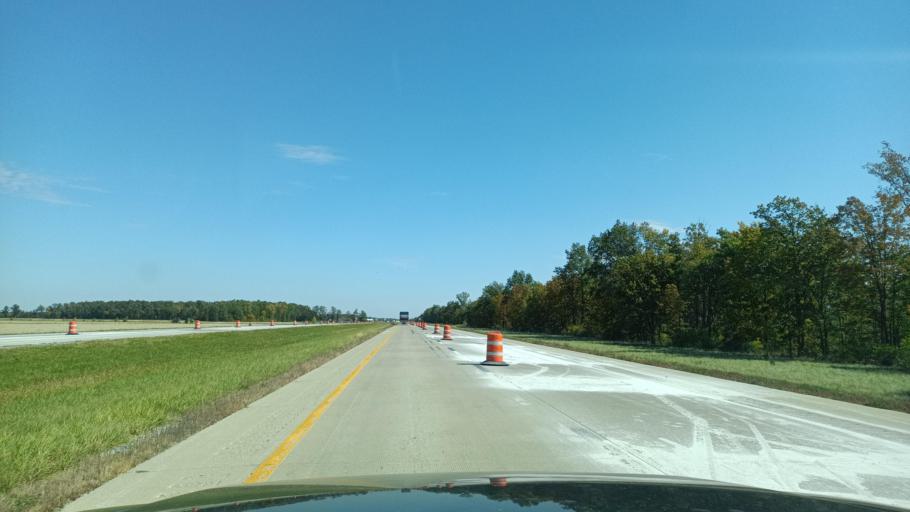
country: US
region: Ohio
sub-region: Paulding County
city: Paulding
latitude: 41.2448
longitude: -84.5011
